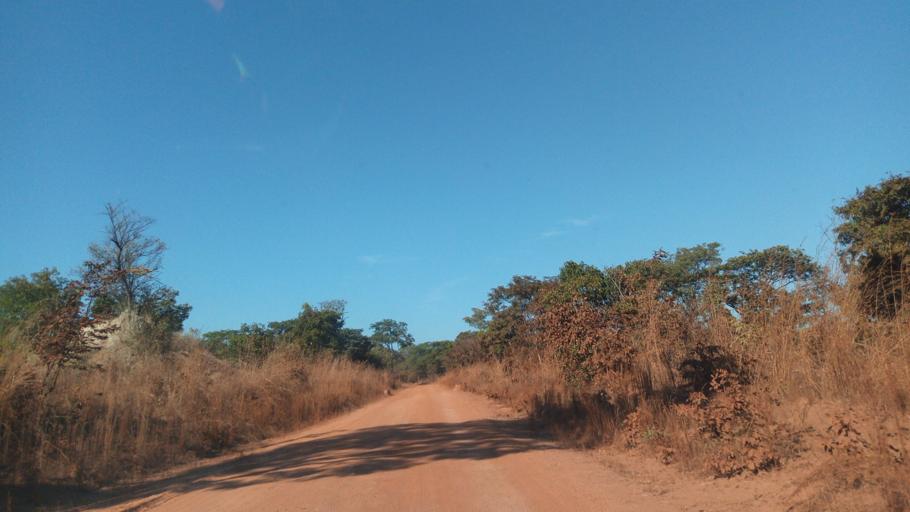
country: ZM
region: Luapula
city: Mwense
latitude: -10.6331
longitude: 28.4100
